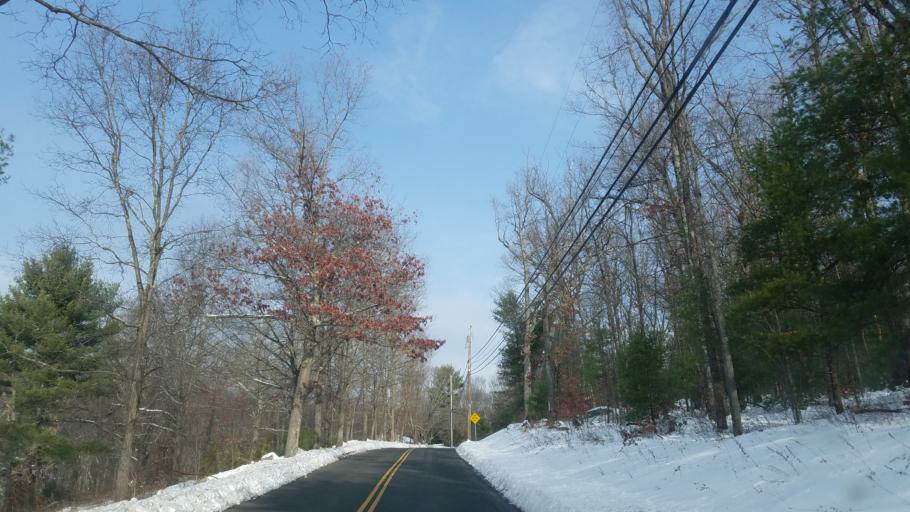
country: US
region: Connecticut
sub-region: Hartford County
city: Canton Valley
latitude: 41.8373
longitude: -72.9049
